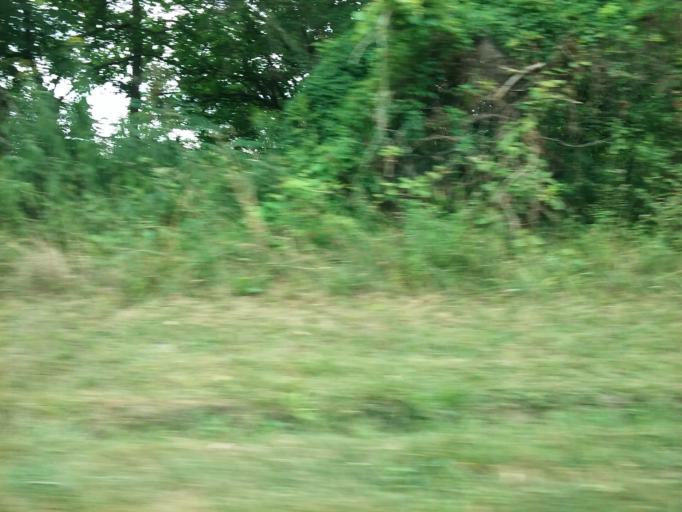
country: US
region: Ohio
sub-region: Hancock County
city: Findlay
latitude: 41.0528
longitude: -83.6735
